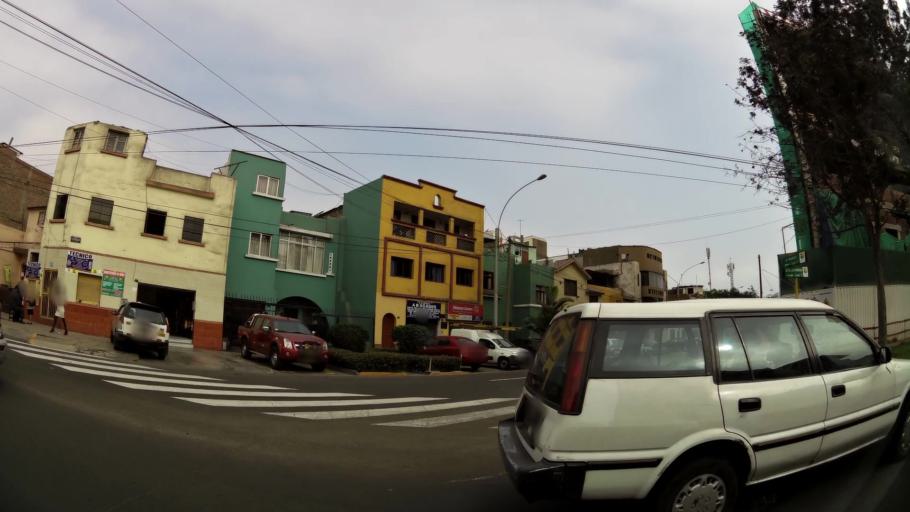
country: PE
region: Lima
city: Lima
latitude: -12.0773
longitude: -77.0474
